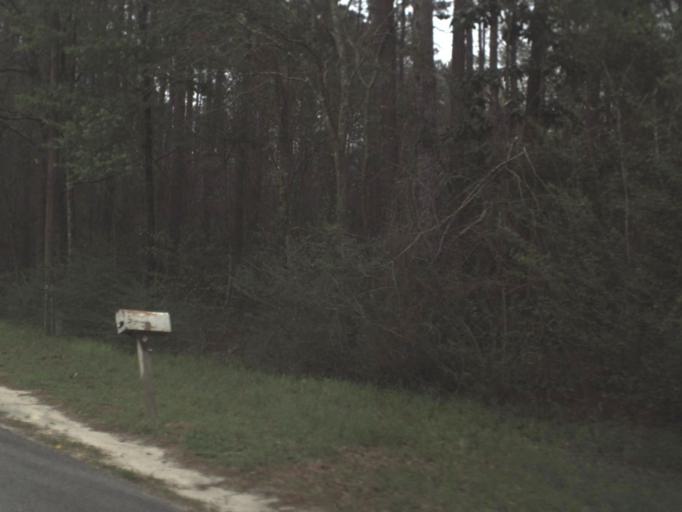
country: US
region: Florida
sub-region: Gadsden County
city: Gretna
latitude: 30.5165
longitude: -84.6974
